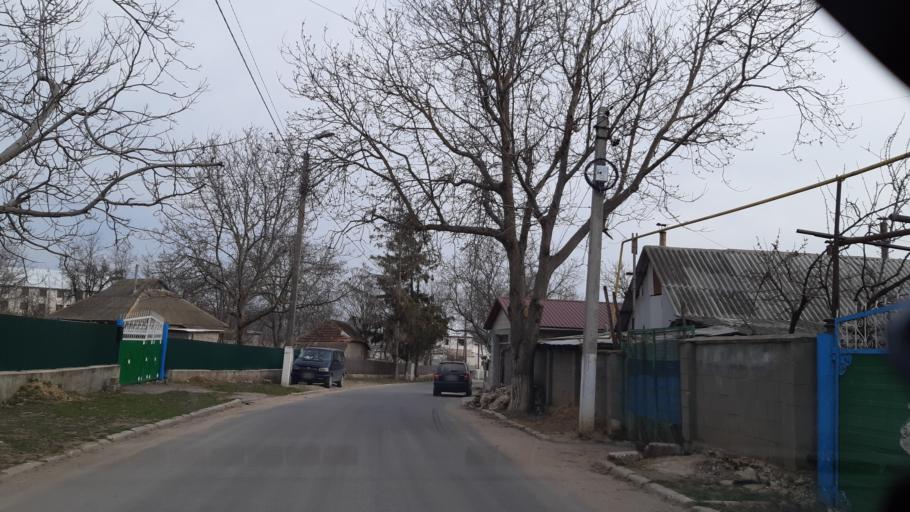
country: MD
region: Soldanesti
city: Soldanesti
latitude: 47.6833
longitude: 28.7802
